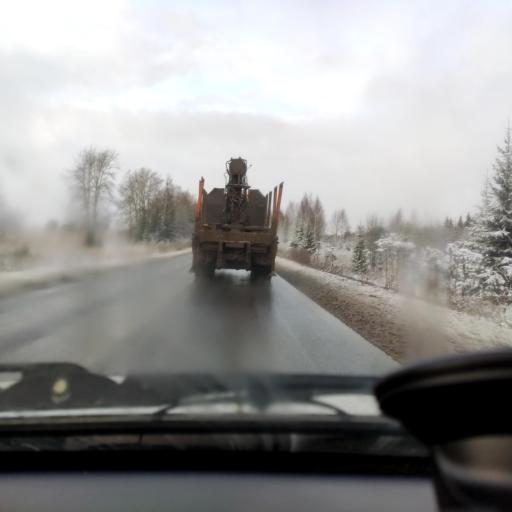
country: RU
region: Perm
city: Nytva
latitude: 57.9403
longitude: 55.3707
